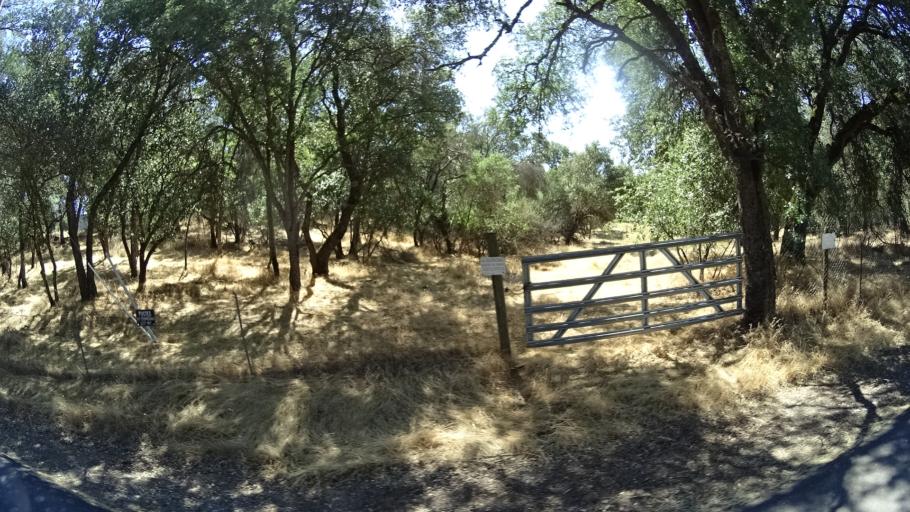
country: US
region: California
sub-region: Calaveras County
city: Angels Camp
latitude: 38.0589
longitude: -120.5393
